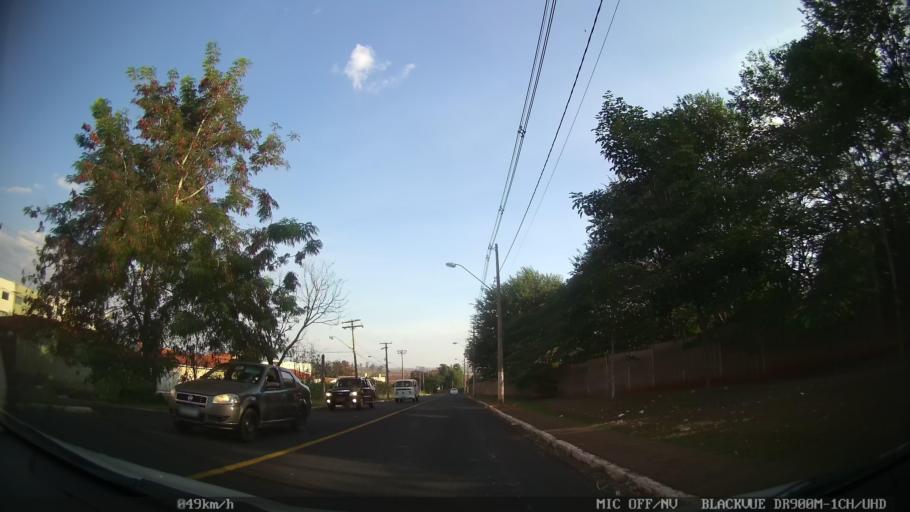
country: BR
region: Sao Paulo
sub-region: Ribeirao Preto
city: Ribeirao Preto
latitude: -21.1662
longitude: -47.8454
